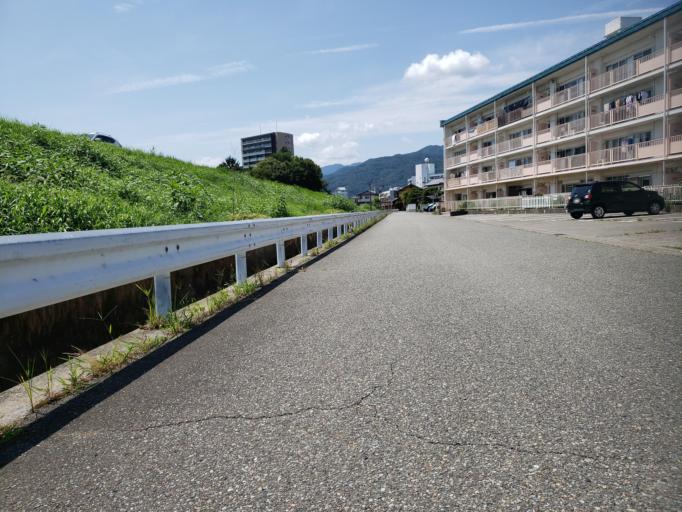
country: JP
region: Nagano
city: Nagano-shi
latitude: 36.6264
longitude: 138.1898
